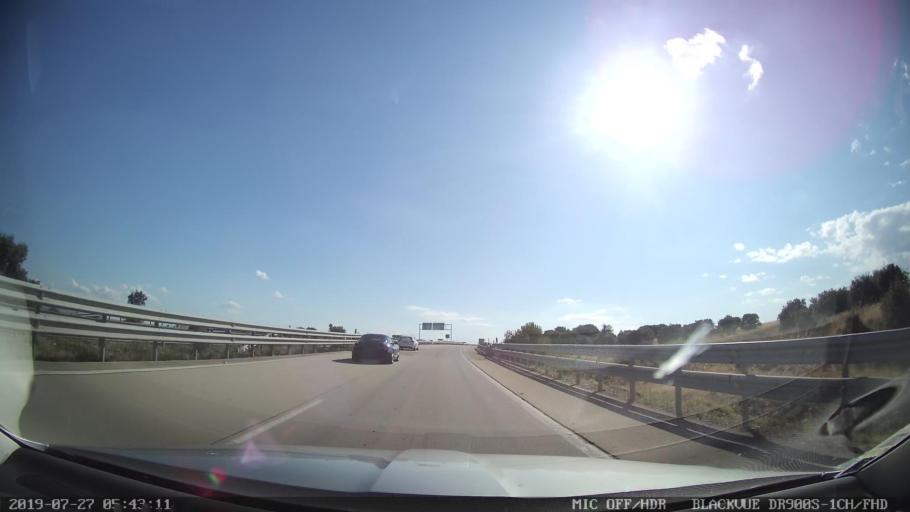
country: ES
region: Castille-La Mancha
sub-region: Province of Toledo
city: Mejorada
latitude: 39.9584
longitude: -4.9063
